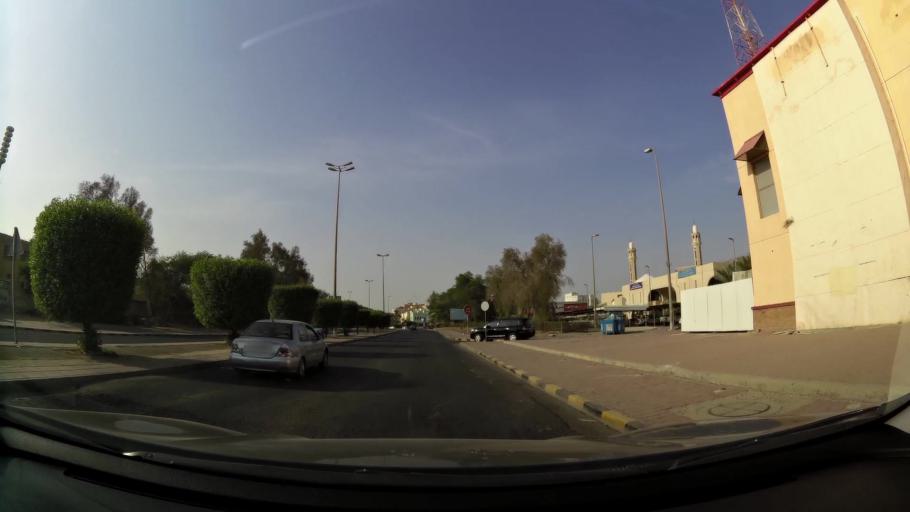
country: KW
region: Mubarak al Kabir
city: Mubarak al Kabir
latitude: 29.1715
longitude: 48.0781
